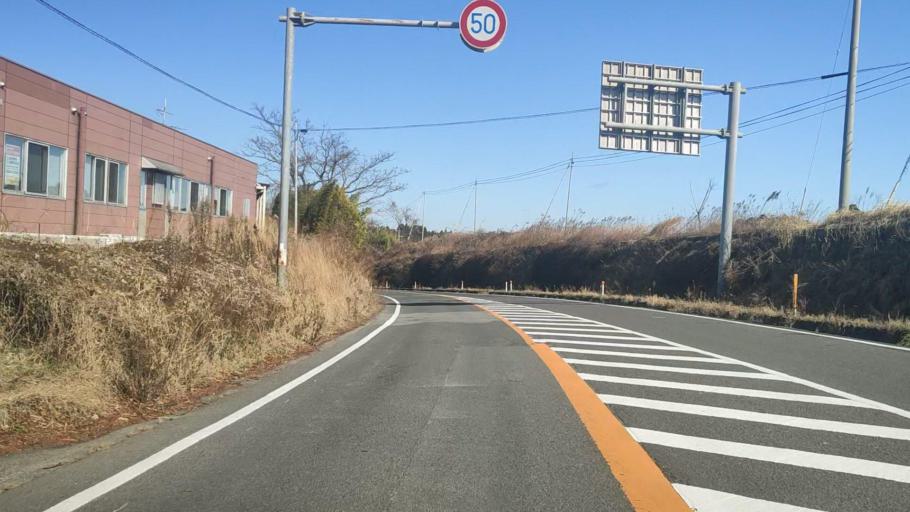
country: JP
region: Kagoshima
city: Sueyoshicho-ninokata
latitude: 31.6898
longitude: 130.9707
